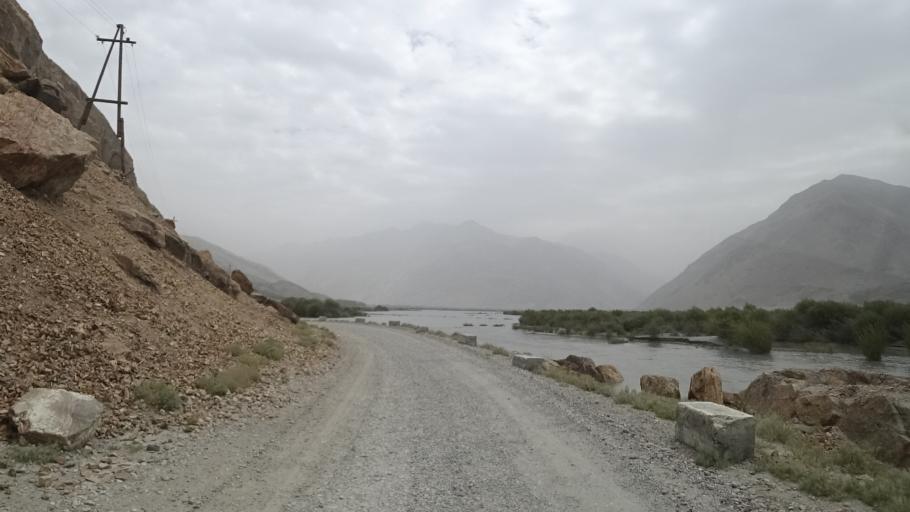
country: AF
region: Badakhshan
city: Khandud
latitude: 37.0232
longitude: 72.6050
